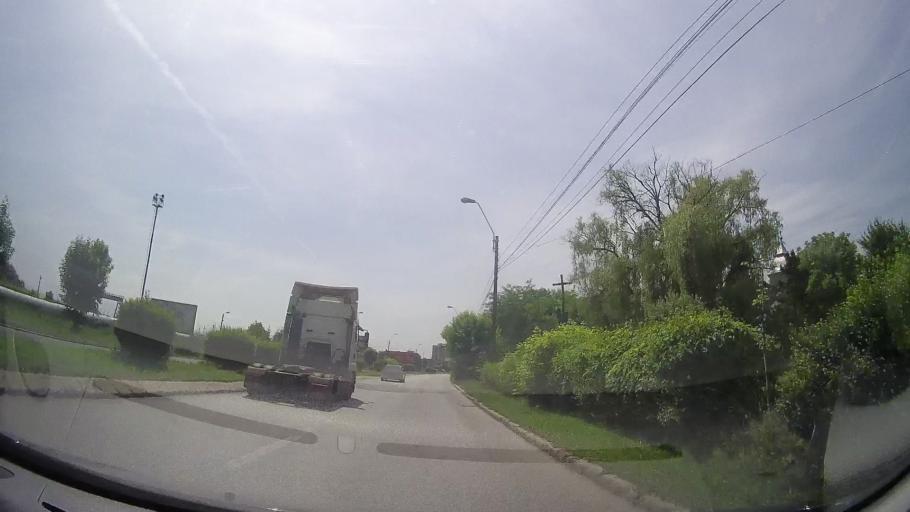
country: RO
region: Hunedoara
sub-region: Municipiul Deva
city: Deva
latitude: 45.8882
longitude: 22.9070
